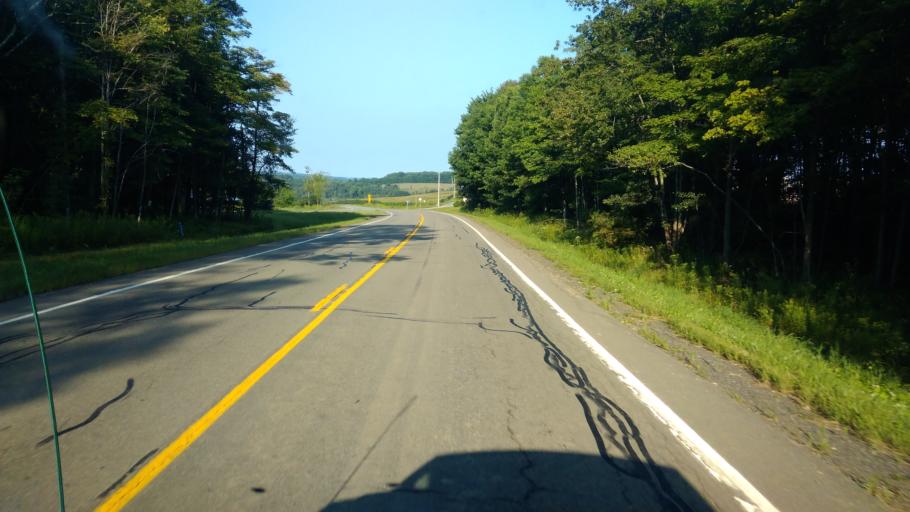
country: US
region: New York
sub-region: Allegany County
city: Andover
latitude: 42.1537
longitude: -77.7113
